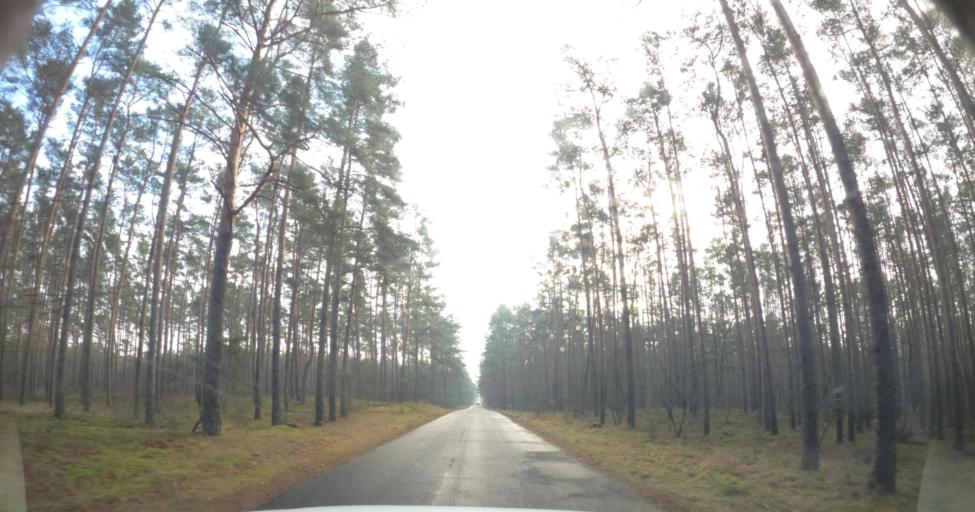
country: PL
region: West Pomeranian Voivodeship
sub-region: Powiat mysliborski
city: Boleszkowice
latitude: 52.6885
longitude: 14.5263
